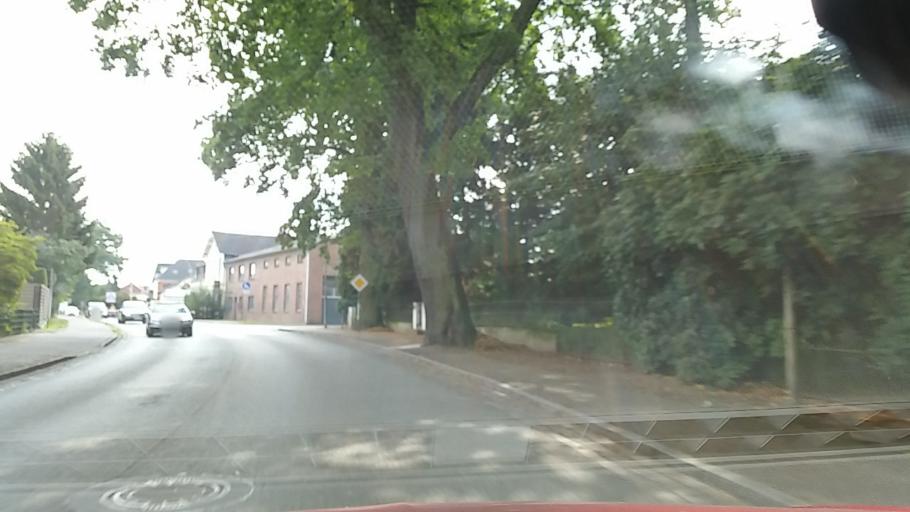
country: DE
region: Schleswig-Holstein
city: Halstenbek
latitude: 53.6020
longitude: 9.8192
